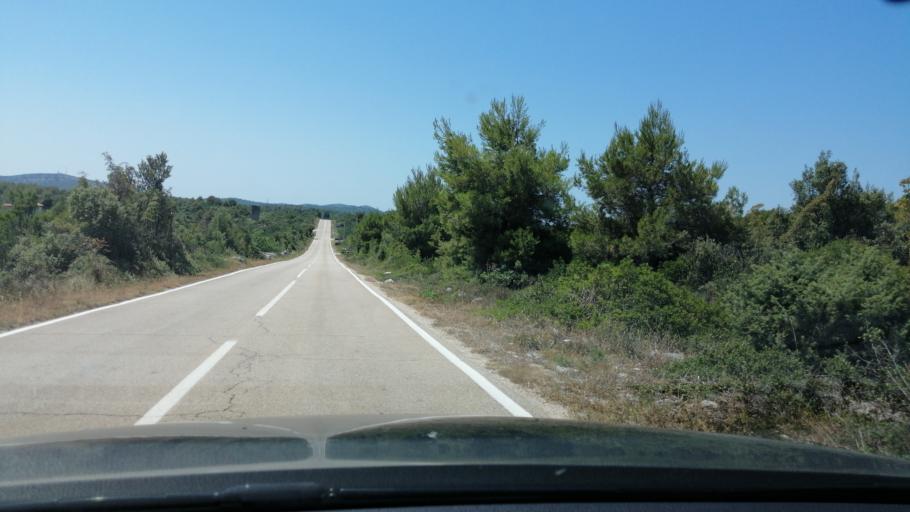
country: HR
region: Sibensko-Kniniska
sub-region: Grad Sibenik
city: Pirovac
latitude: 43.8360
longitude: 15.6877
